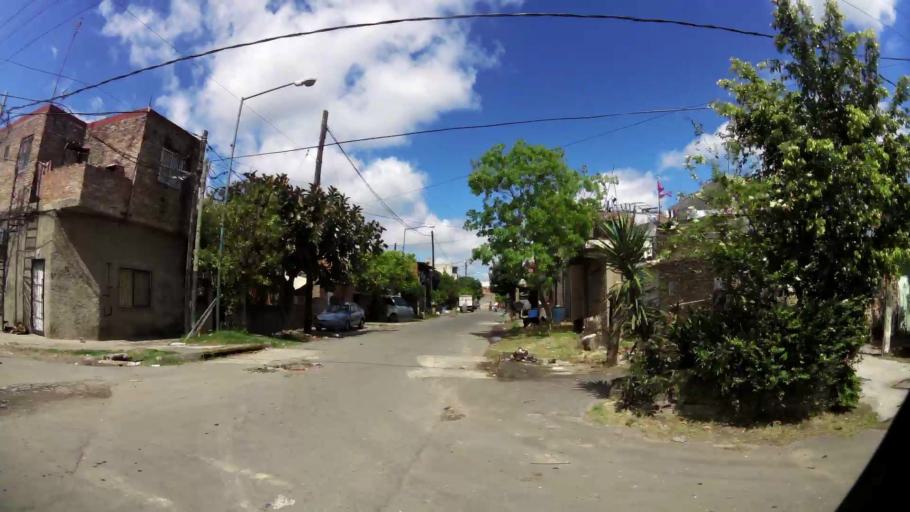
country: AR
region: Buenos Aires F.D.
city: Villa Lugano
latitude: -34.6765
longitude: -58.4305
